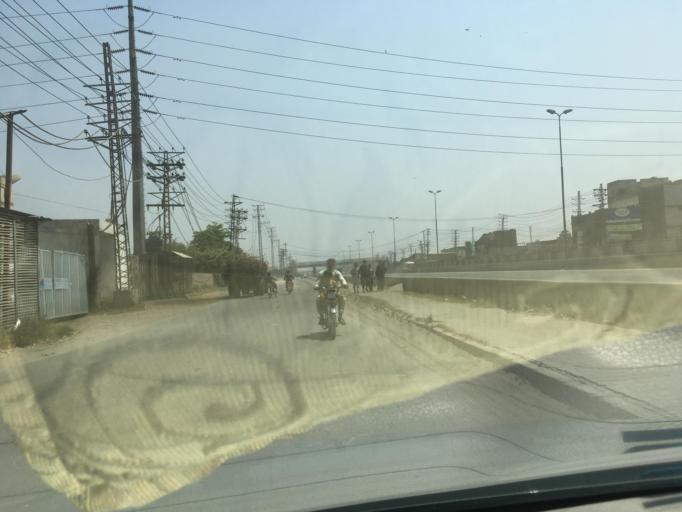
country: PK
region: Punjab
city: Lahore
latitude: 31.6089
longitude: 74.3553
